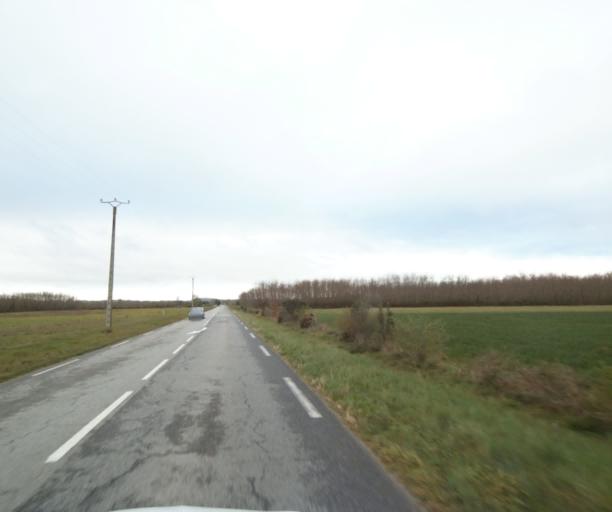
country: FR
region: Midi-Pyrenees
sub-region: Departement de l'Ariege
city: Saverdun
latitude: 43.2315
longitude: 1.6214
